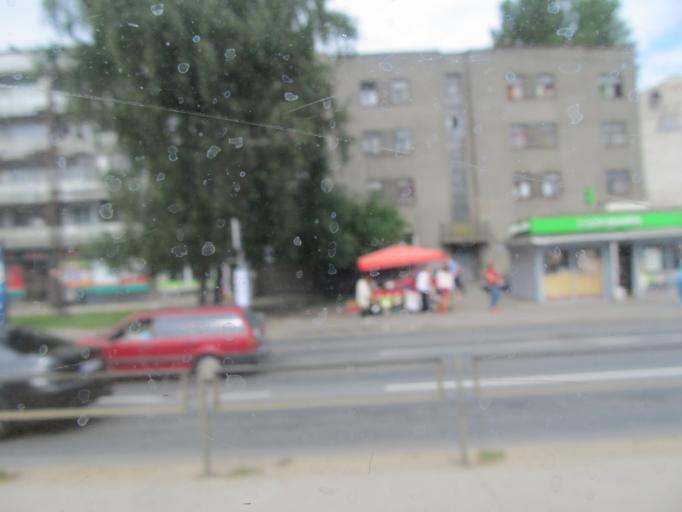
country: LV
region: Riga
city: Riga
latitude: 56.9415
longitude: 24.0950
